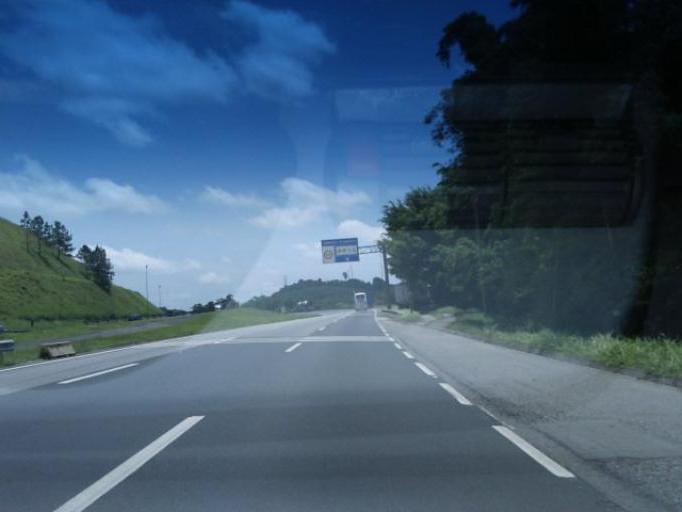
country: BR
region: Sao Paulo
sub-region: Juquia
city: Juquia
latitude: -24.3875
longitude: -47.7185
